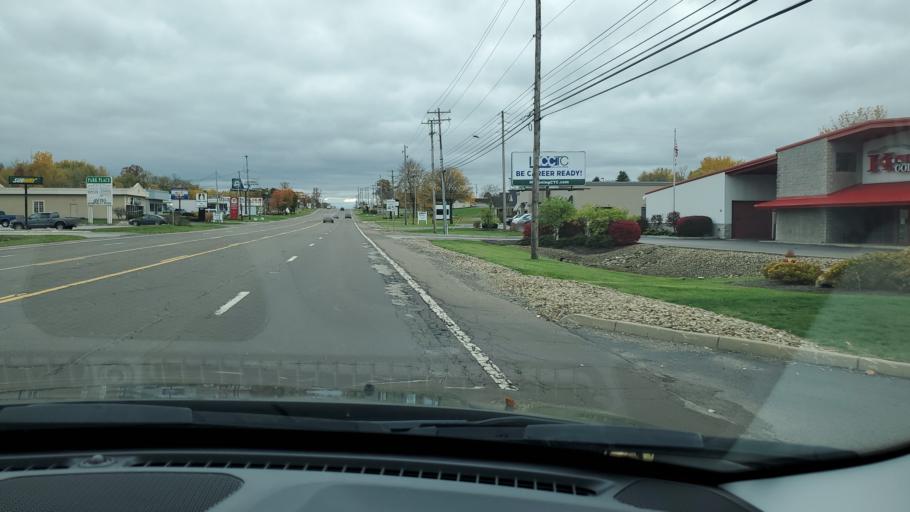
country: US
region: Ohio
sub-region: Mahoning County
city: Boardman
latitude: 41.0052
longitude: -80.6629
